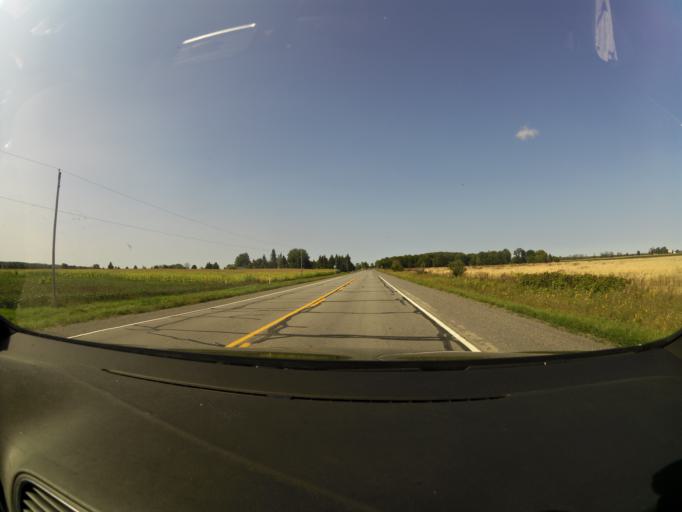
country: CA
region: Ontario
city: Arnprior
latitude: 45.3478
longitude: -76.2953
